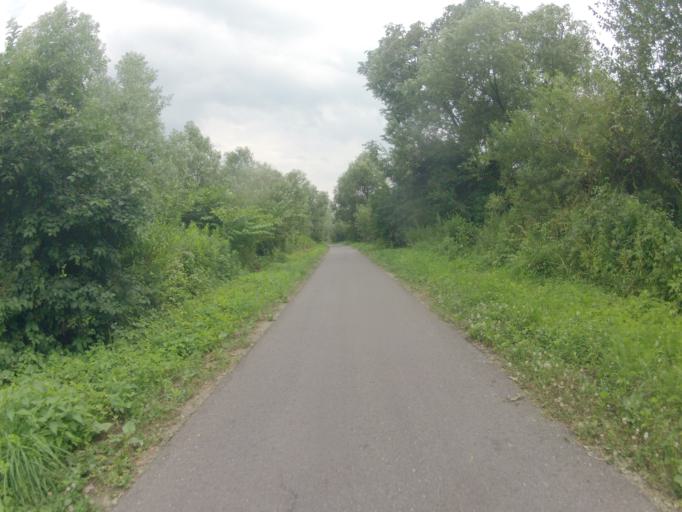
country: PL
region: Lesser Poland Voivodeship
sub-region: Powiat nowosadecki
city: Stary Sacz
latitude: 49.5473
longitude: 20.6535
